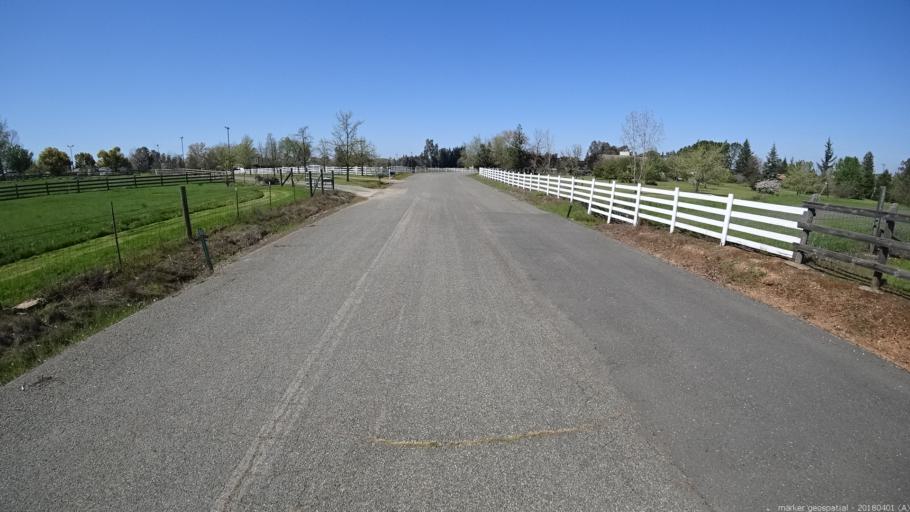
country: US
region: California
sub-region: Sacramento County
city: Wilton
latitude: 38.4137
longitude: -121.2177
